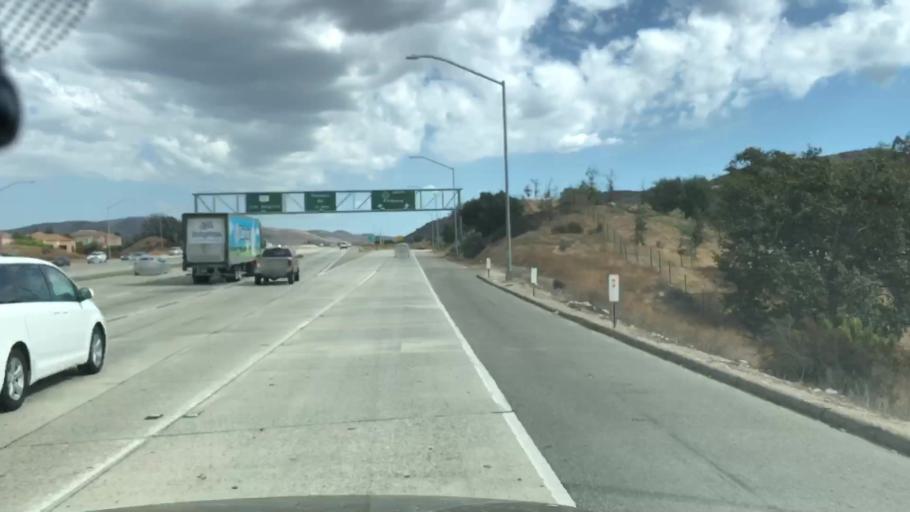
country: US
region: California
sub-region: Ventura County
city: Thousand Oaks
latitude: 34.1765
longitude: -118.8676
